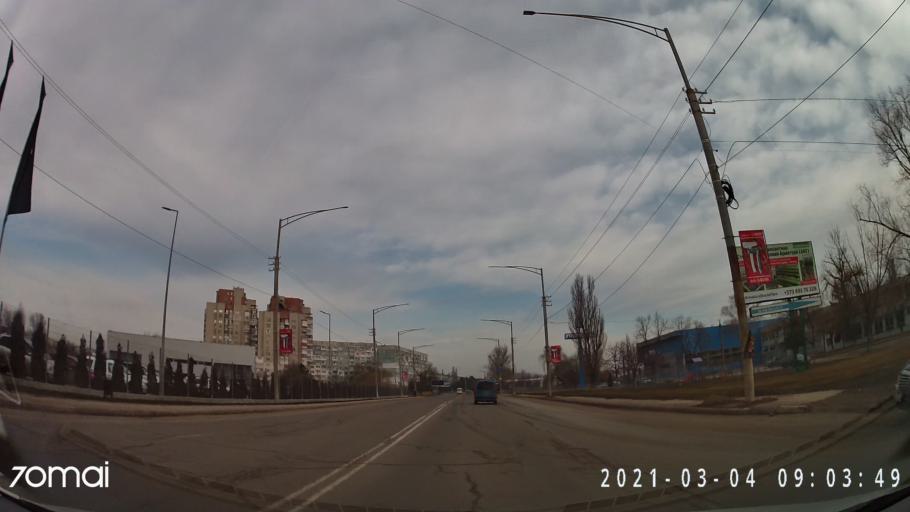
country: MD
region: Balti
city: Balti
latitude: 47.7536
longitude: 27.9425
